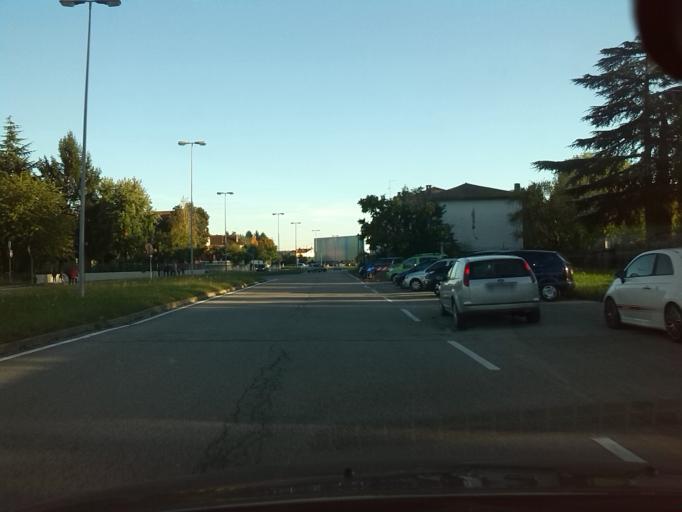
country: IT
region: Friuli Venezia Giulia
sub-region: Provincia di Udine
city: Colugna
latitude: 46.0774
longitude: 13.2023
